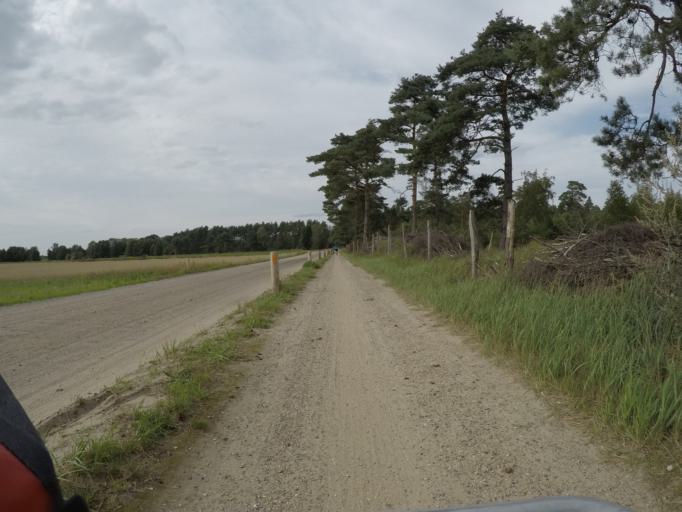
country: DE
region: Lower Saxony
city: Bardowick
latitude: 53.3130
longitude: 10.4012
